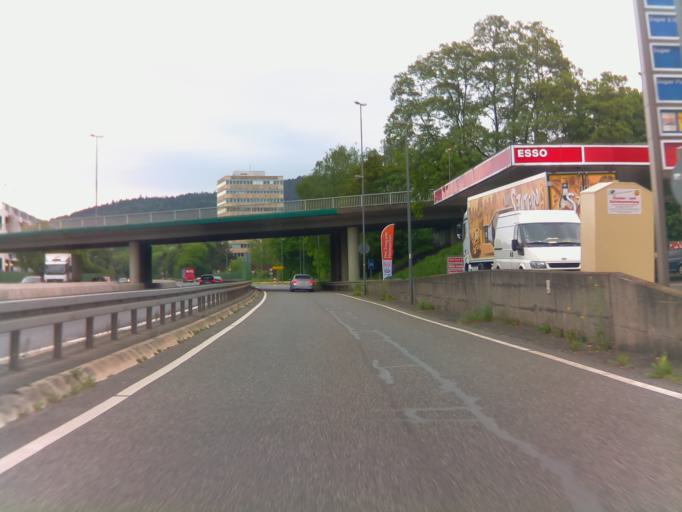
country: DE
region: Hesse
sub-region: Regierungsbezirk Giessen
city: Marburg an der Lahn
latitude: 50.8058
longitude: 8.7783
